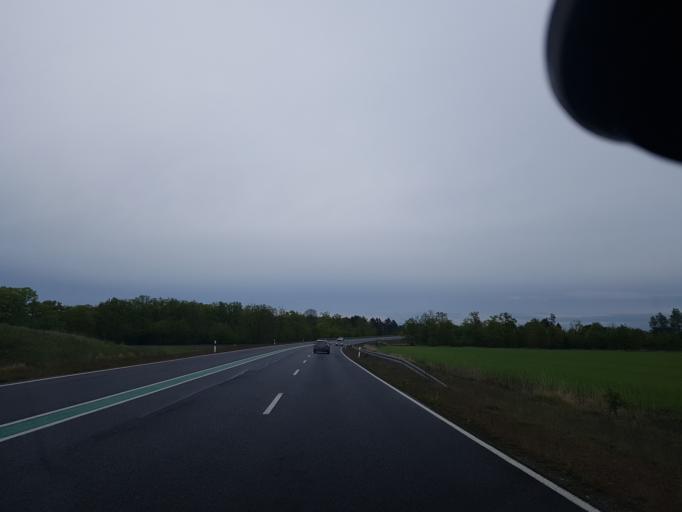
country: DE
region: Brandenburg
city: Drebkau
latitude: 51.6356
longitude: 14.1958
